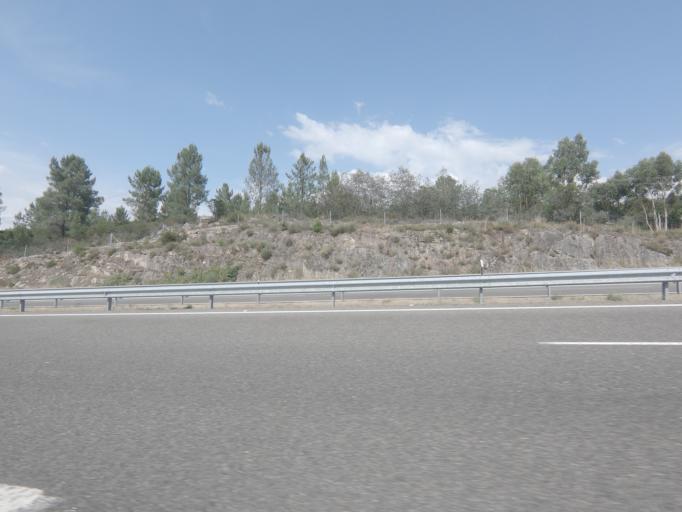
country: ES
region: Galicia
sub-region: Provincia de Ourense
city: Ourense
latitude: 42.2865
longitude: -7.8751
